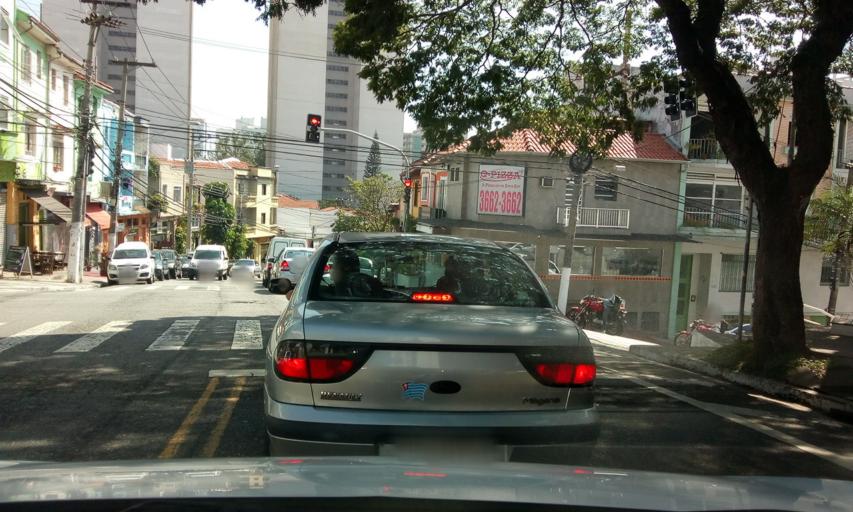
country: BR
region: Sao Paulo
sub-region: Sao Paulo
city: Sao Paulo
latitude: -23.5399
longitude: -46.6830
